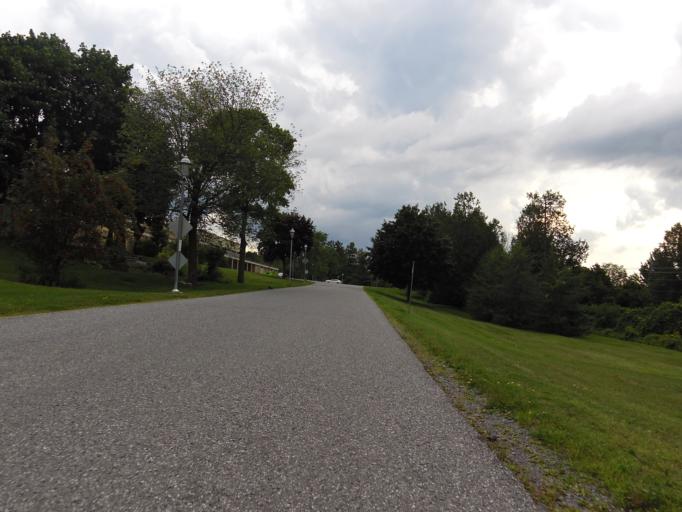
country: CA
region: Ontario
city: Bells Corners
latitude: 45.3270
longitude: -75.8087
